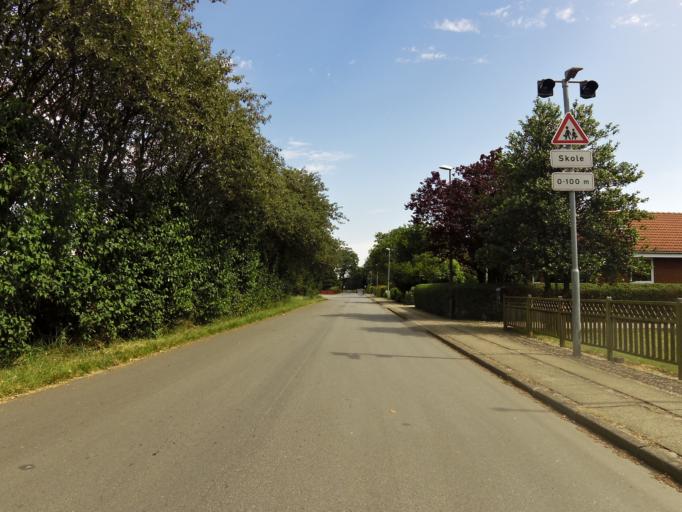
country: DK
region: South Denmark
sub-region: Haderslev Kommune
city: Vojens
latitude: 55.1974
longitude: 9.2025
